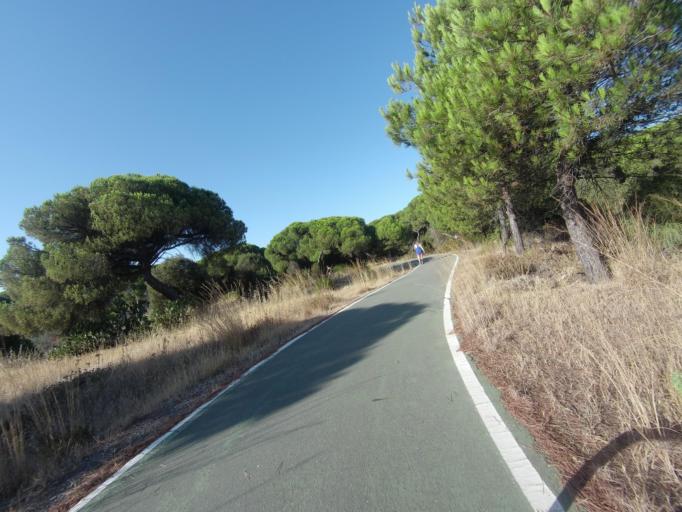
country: ES
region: Andalusia
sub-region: Provincia de Huelva
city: Aljaraque
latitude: 37.2090
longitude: -7.0281
